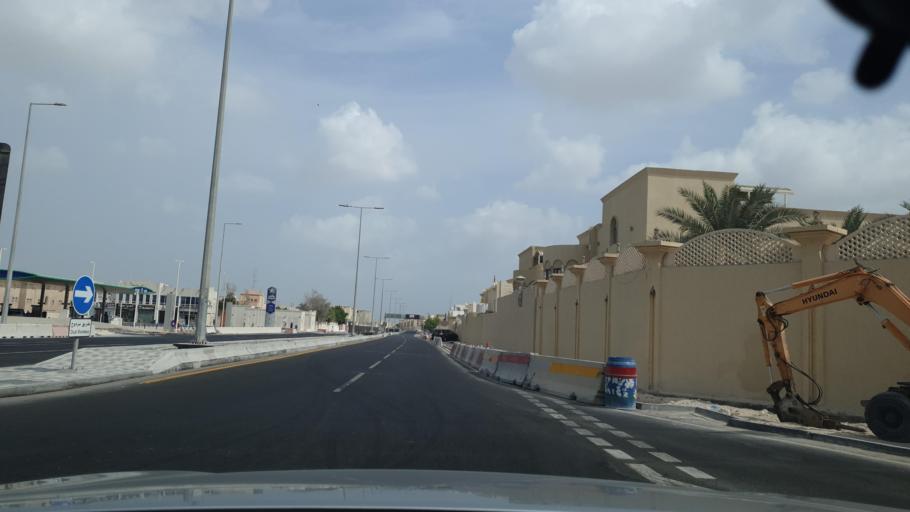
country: QA
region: Baladiyat ar Rayyan
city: Ar Rayyan
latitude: 25.2728
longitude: 51.4372
